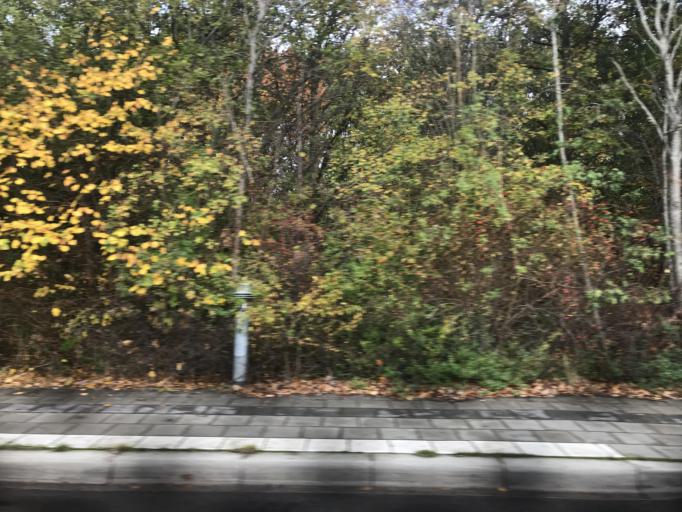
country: SE
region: Skane
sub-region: Landskrona
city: Landskrona
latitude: 55.8934
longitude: 12.8491
